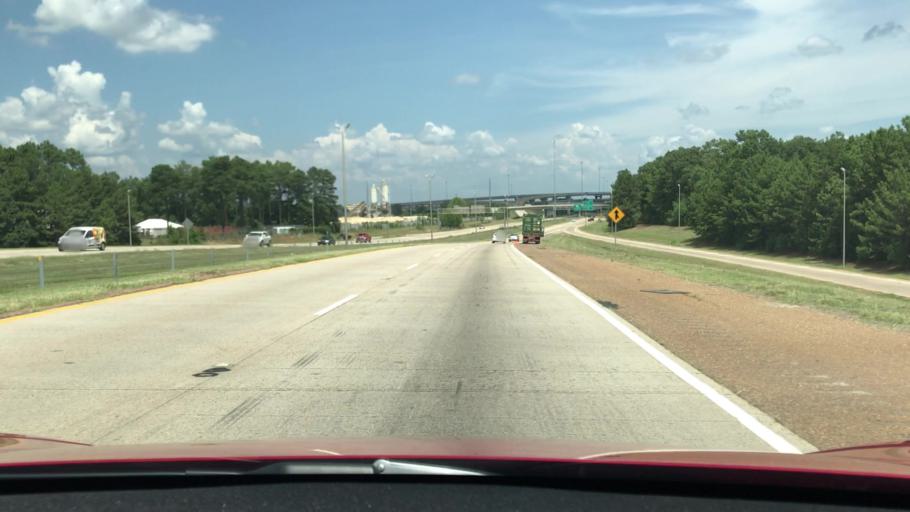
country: US
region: Louisiana
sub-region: Bossier Parish
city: Bossier City
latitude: 32.4204
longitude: -93.7621
